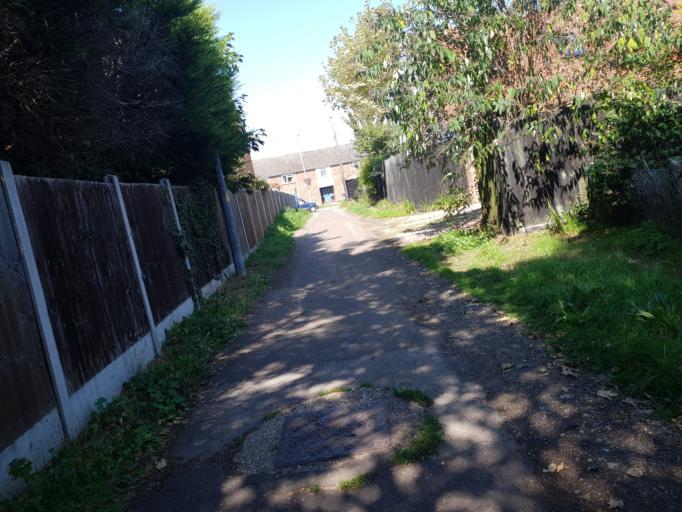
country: GB
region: England
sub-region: Suffolk
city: East Bergholt
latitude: 51.9255
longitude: 0.9830
